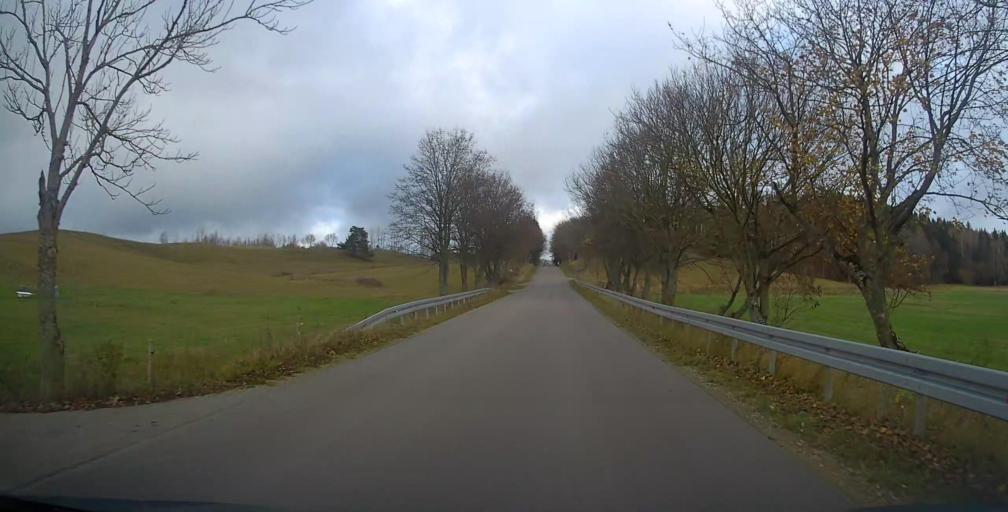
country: PL
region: Podlasie
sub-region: Suwalki
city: Suwalki
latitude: 54.3070
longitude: 22.8801
